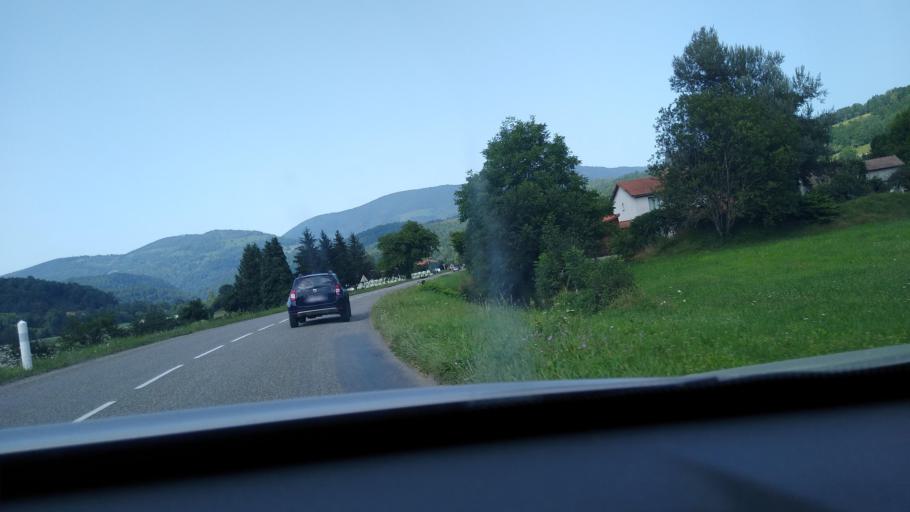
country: FR
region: Midi-Pyrenees
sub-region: Departement de l'Ariege
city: Saint-Girons
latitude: 42.8730
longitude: 1.2114
